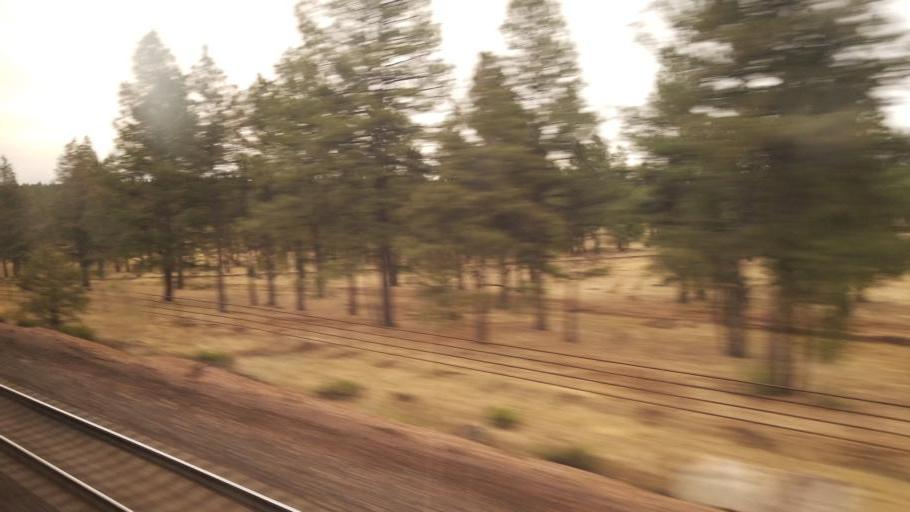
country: US
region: Arizona
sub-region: Coconino County
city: Parks
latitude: 35.2357
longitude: -112.0017
